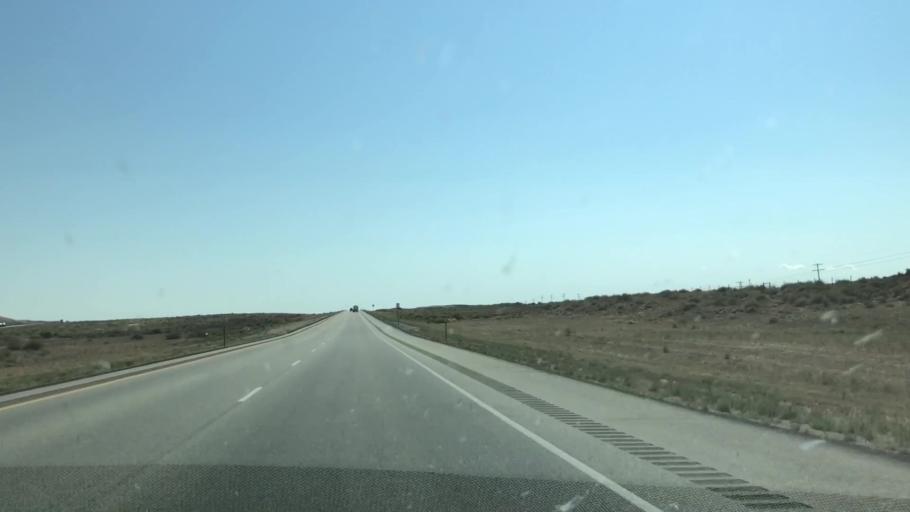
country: US
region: Wyoming
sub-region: Carbon County
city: Rawlins
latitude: 41.7051
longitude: -107.8592
